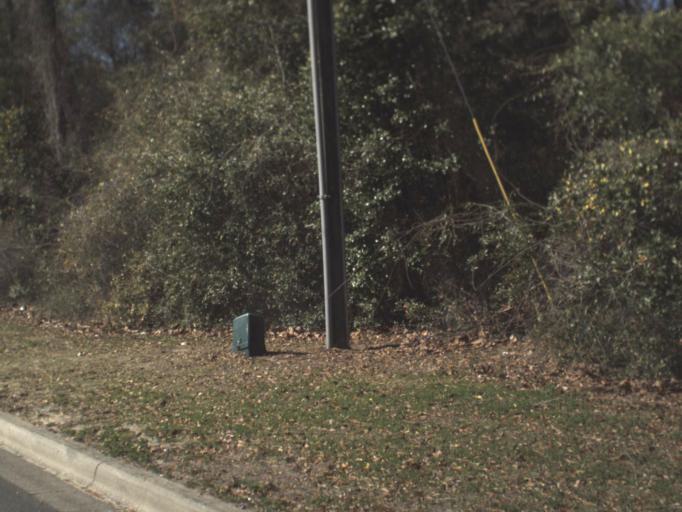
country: US
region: Florida
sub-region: Leon County
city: Tallahassee
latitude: 30.4191
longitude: -84.3506
